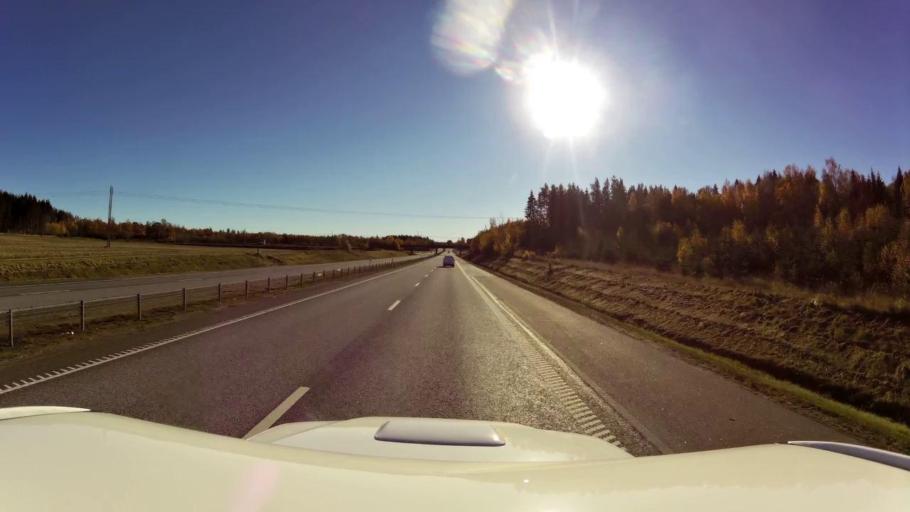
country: SE
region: OEstergoetland
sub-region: Linkopings Kommun
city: Malmslatt
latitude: 58.4172
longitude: 15.5430
